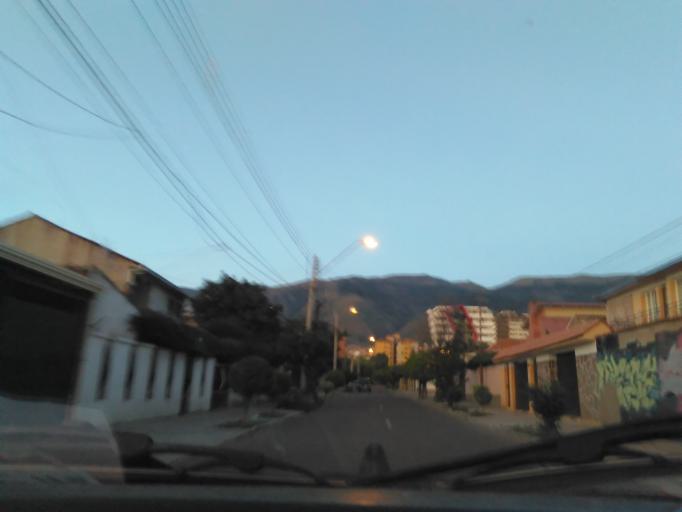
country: BO
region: Cochabamba
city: Cochabamba
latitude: -17.3721
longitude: -66.1659
